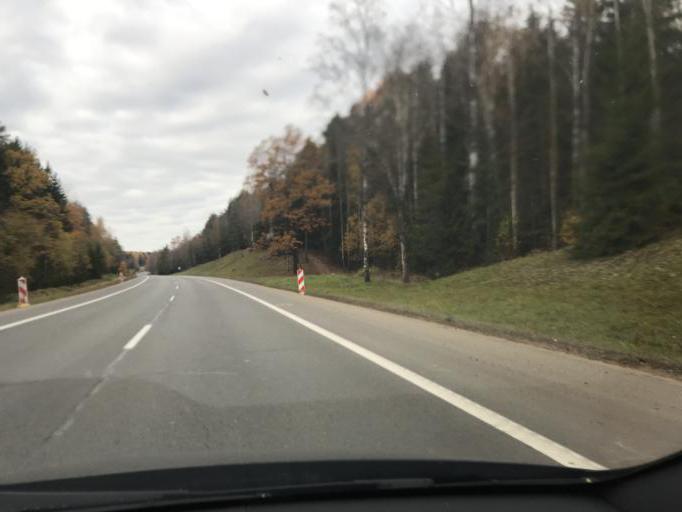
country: BY
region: Minsk
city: Slabada
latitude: 54.0361
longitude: 27.8370
